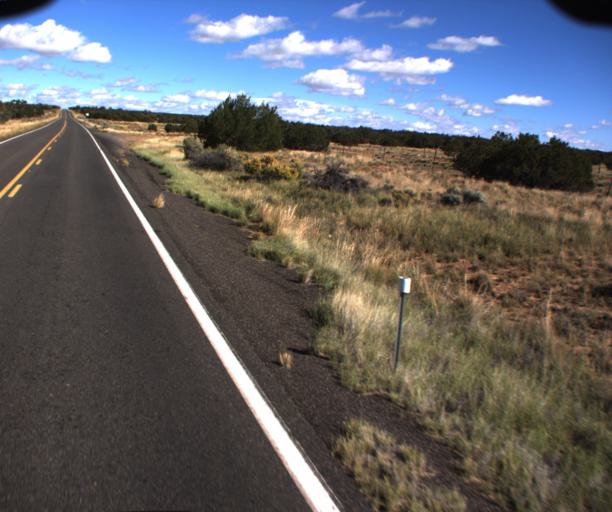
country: US
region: Arizona
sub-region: Apache County
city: Saint Johns
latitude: 34.8228
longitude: -109.2374
